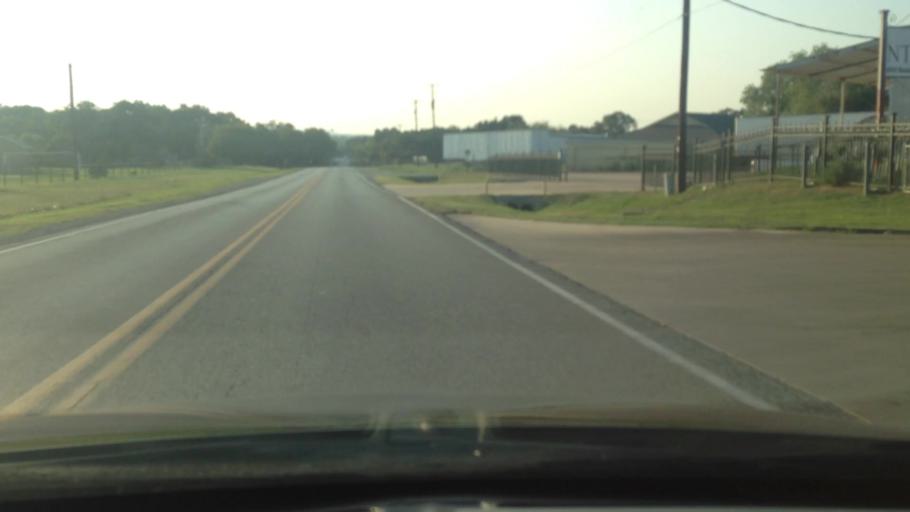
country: US
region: Texas
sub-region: Tarrant County
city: Rendon
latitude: 32.5935
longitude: -97.2548
